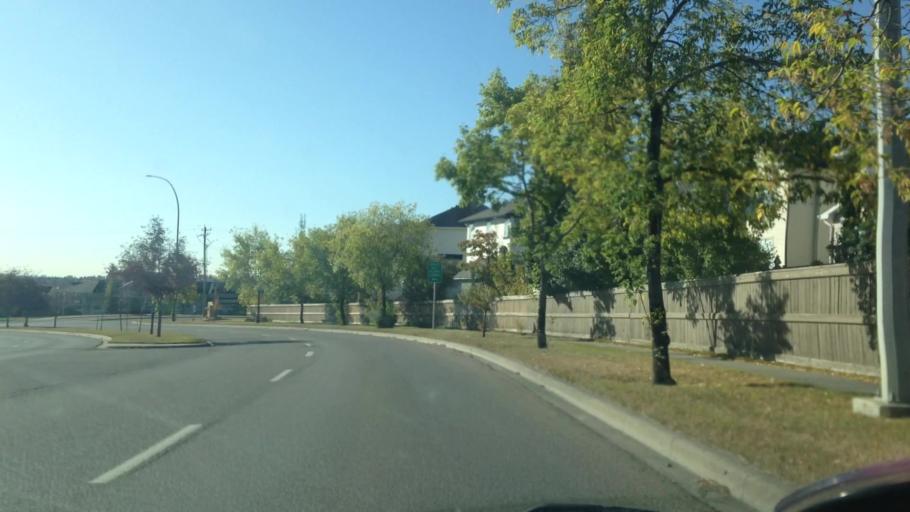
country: CA
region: Alberta
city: Calgary
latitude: 51.1446
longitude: -114.0729
